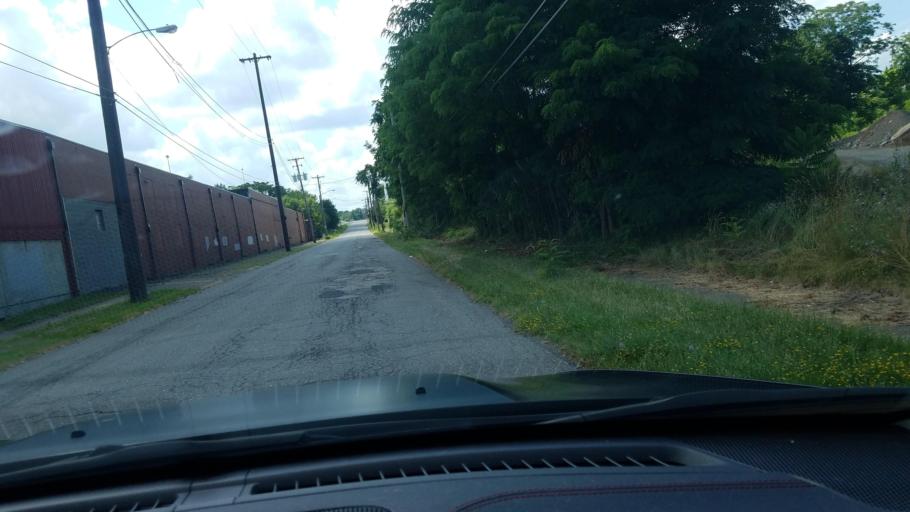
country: US
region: Ohio
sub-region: Mahoning County
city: Youngstown
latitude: 41.1009
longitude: -80.6596
